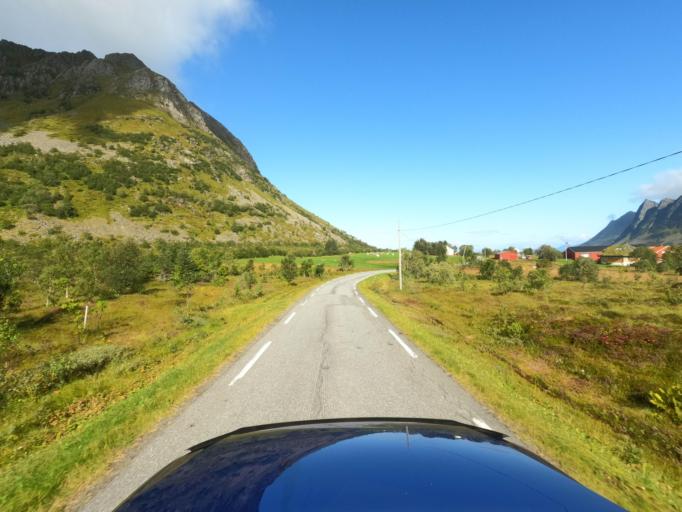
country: NO
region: Nordland
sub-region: Vagan
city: Kabelvag
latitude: 68.2928
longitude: 14.2645
